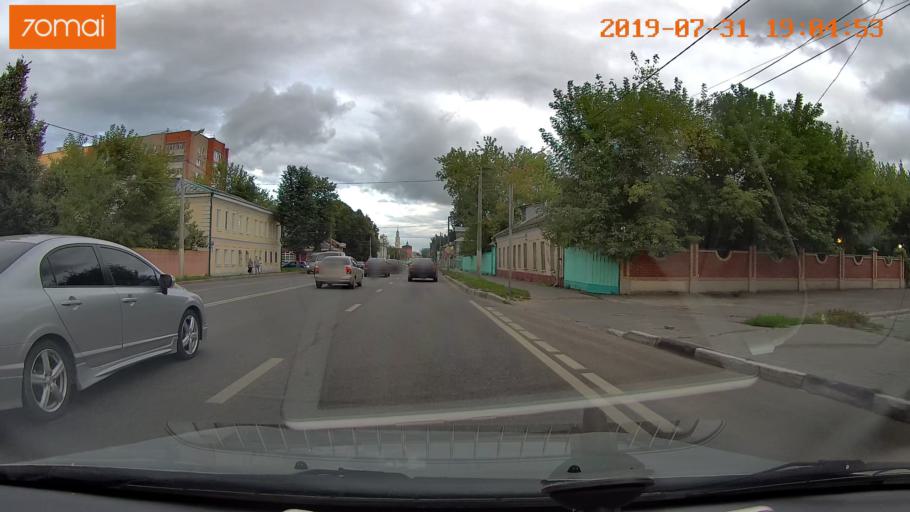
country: RU
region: Moskovskaya
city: Raduzhnyy
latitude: 55.1078
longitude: 38.7430
